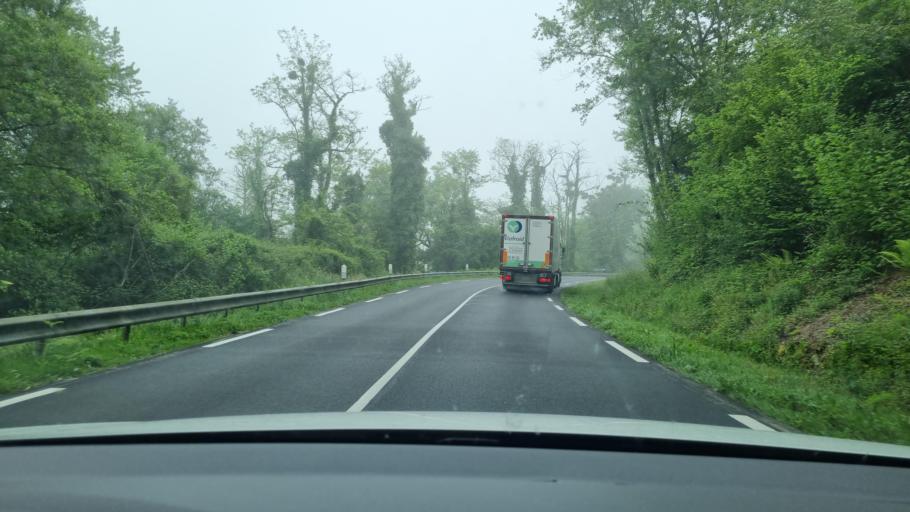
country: FR
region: Aquitaine
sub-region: Departement des Pyrenees-Atlantiques
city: Orthez
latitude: 43.5212
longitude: -0.7183
